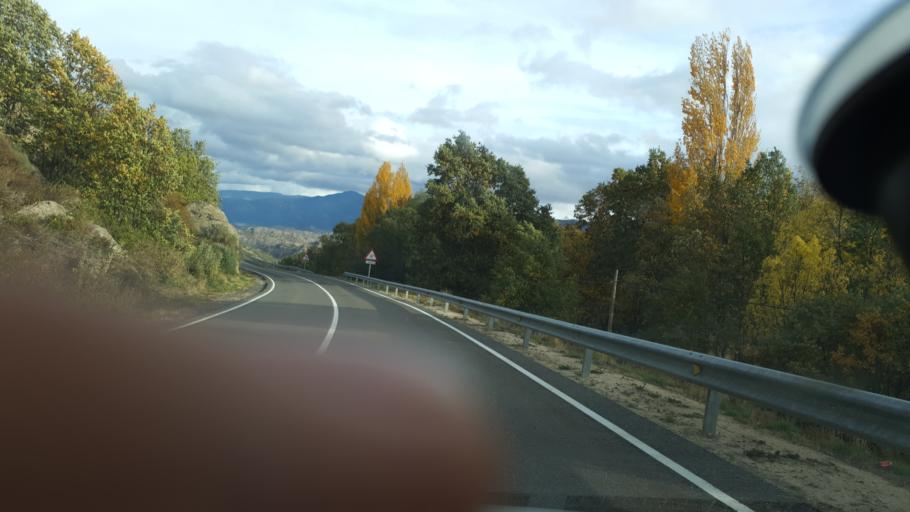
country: ES
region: Castille and Leon
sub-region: Provincia de Avila
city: Navalosa
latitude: 40.3941
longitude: -4.9111
